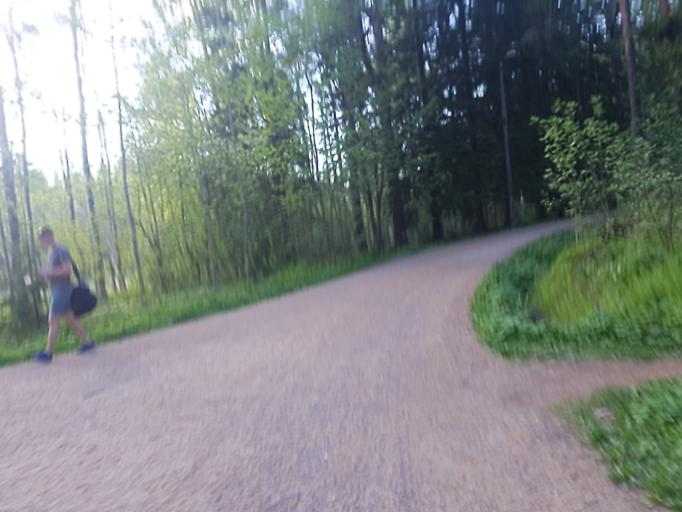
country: FI
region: Uusimaa
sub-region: Helsinki
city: Helsinki
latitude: 60.2298
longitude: 24.9064
